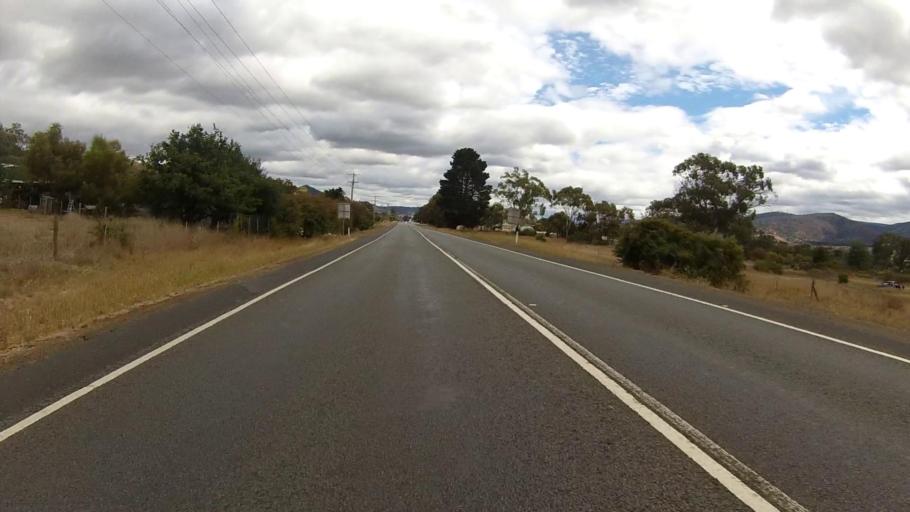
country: AU
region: Tasmania
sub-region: Brighton
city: Bridgewater
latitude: -42.6777
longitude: 147.2641
